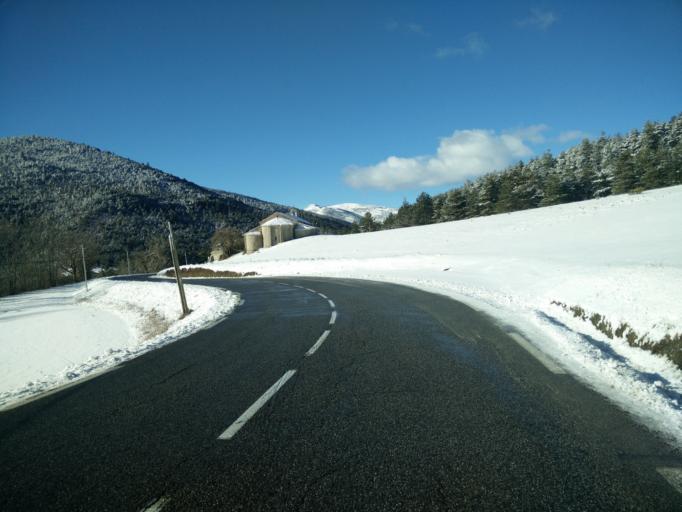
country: FR
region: Provence-Alpes-Cote d'Azur
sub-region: Departement des Alpes-de-Haute-Provence
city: Annot
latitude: 43.9129
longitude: 6.5977
